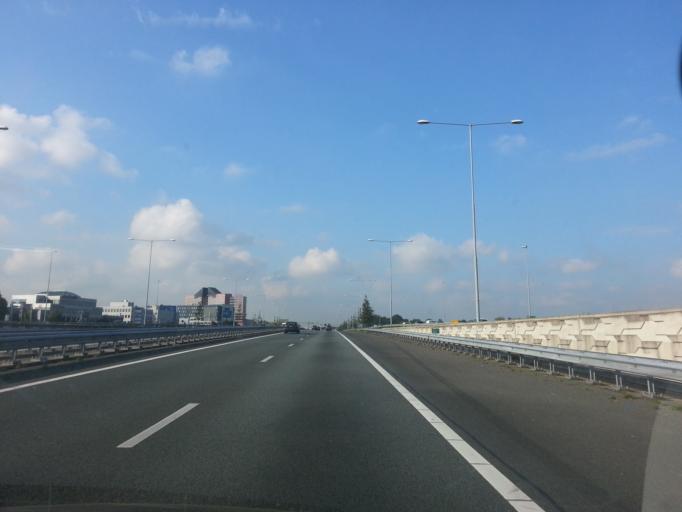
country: NL
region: North Brabant
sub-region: Gemeente 's-Hertogenbosch
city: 's-Hertogenbosch
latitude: 51.7085
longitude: 5.3462
